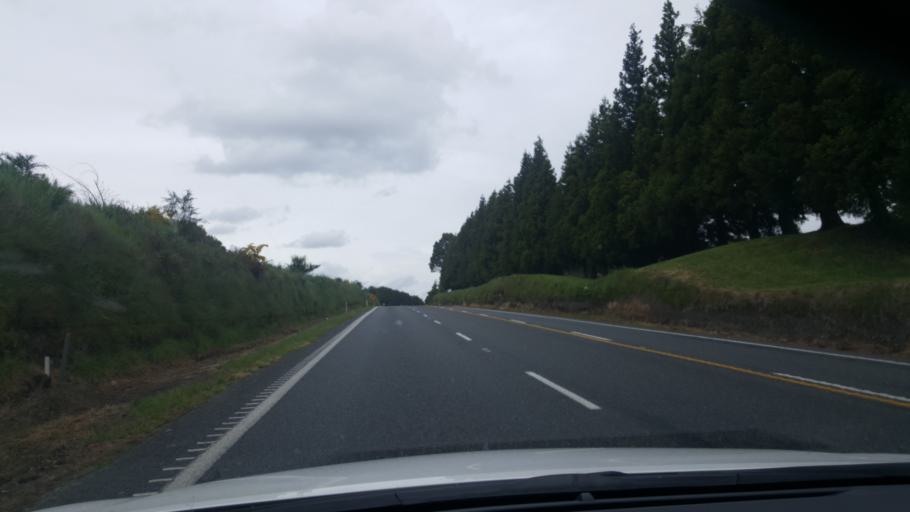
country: NZ
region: Bay of Plenty
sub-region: Rotorua District
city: Rotorua
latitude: -38.2460
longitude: 176.3131
